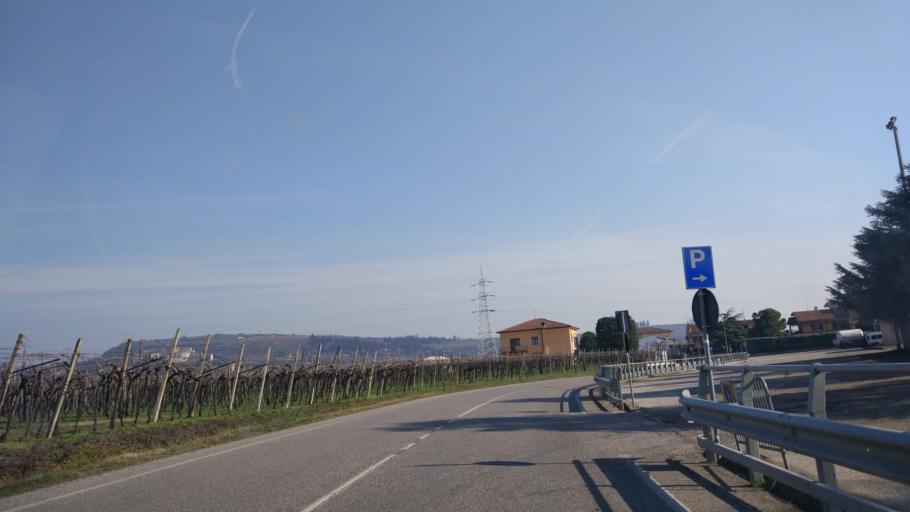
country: IT
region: Veneto
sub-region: Provincia di Verona
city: Soave
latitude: 45.4162
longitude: 11.2332
